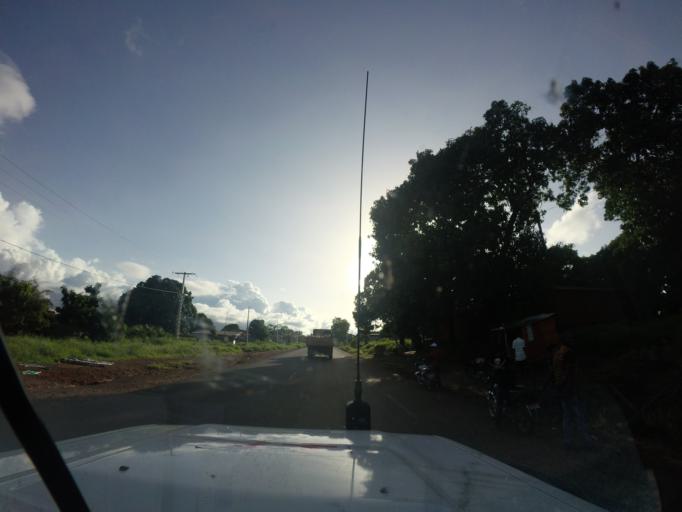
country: GN
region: Kindia
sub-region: Kindia
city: Kindia
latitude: 10.0322
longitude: -12.8537
